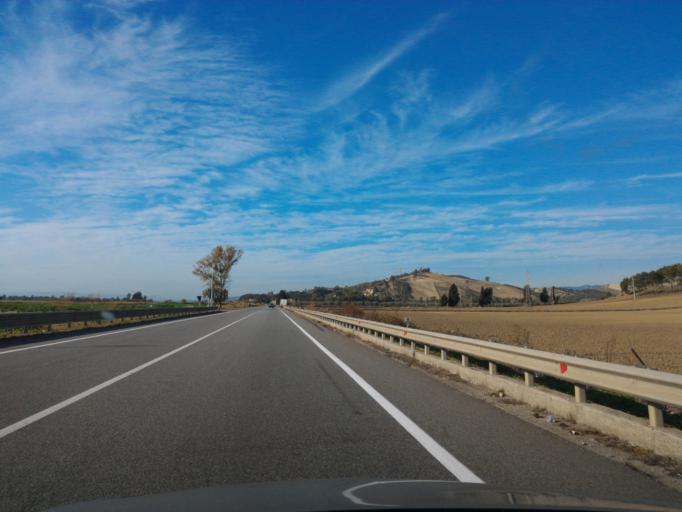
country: IT
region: Calabria
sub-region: Provincia di Catanzaro
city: Botricello
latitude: 38.9429
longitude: 16.8984
